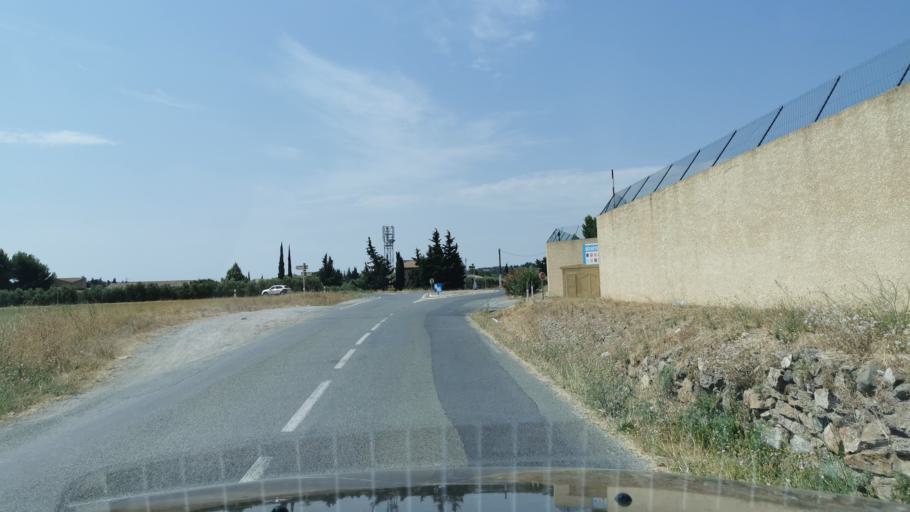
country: FR
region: Languedoc-Roussillon
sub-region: Departement de l'Aude
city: Ginestas
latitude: 43.2764
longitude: 2.8866
